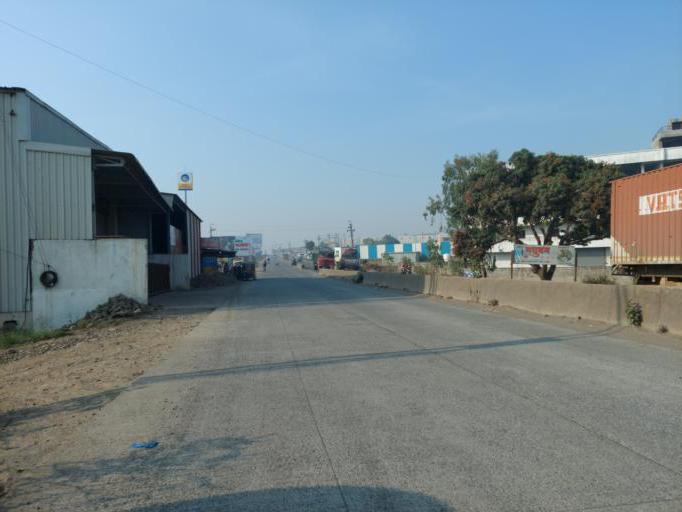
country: IN
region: Maharashtra
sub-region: Pune Division
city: Pune
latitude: 18.4627
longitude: 73.9515
